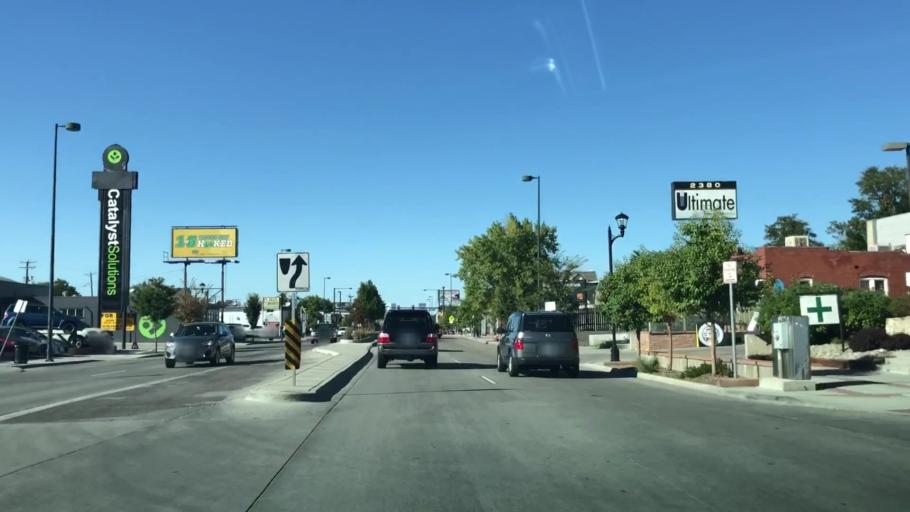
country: US
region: Colorado
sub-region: Arapahoe County
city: Englewood
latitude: 39.6731
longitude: -104.9875
